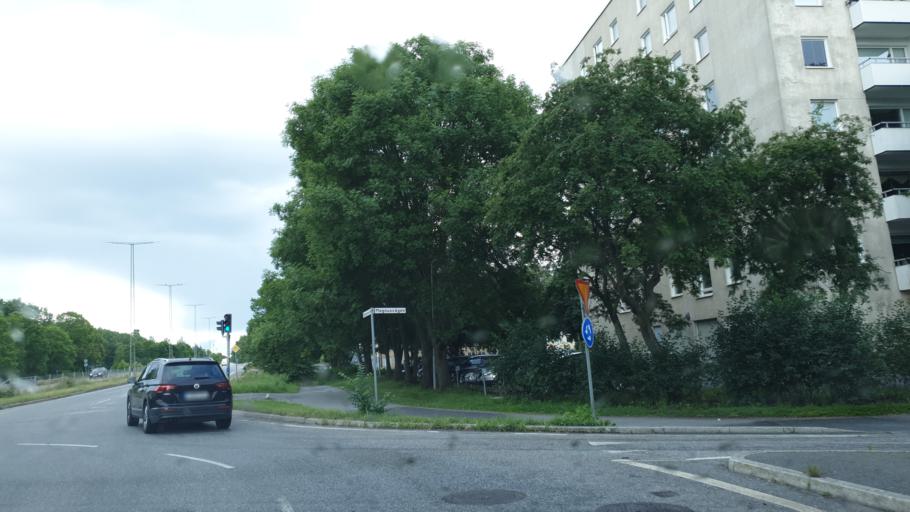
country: SE
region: Stockholm
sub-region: Jarfalla Kommun
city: Jakobsberg
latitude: 59.4251
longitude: 17.8423
